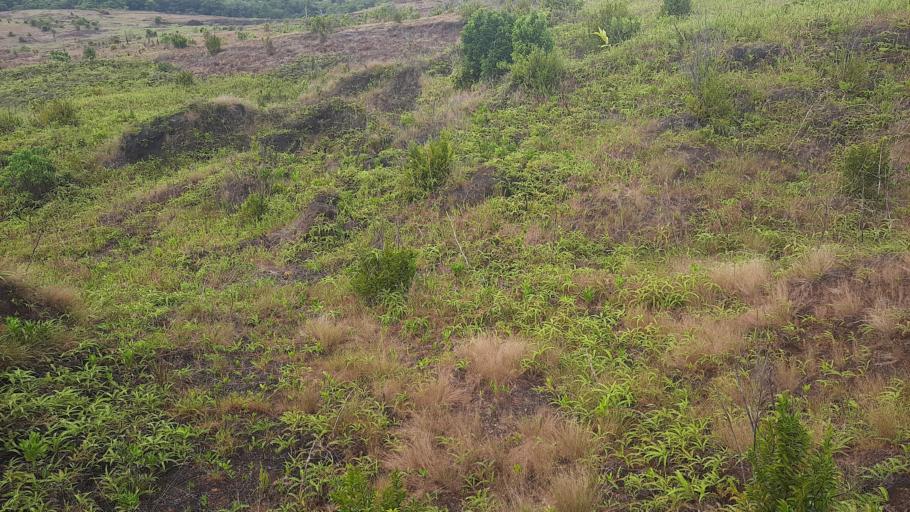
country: PW
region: Aimeliik
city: Ngchemiangel
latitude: 7.4487
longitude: 134.5347
